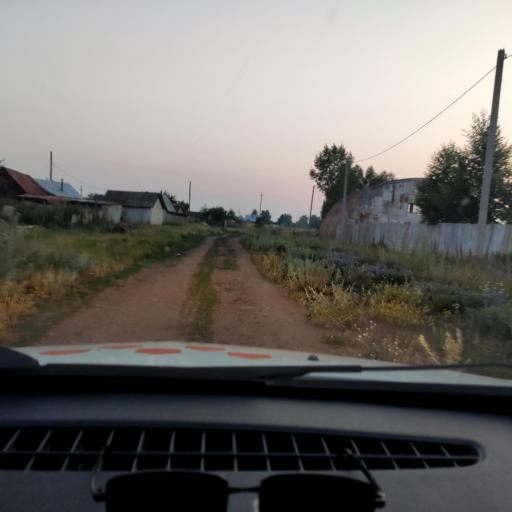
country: RU
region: Bashkortostan
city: Ulukulevo
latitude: 54.3694
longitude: 56.4311
